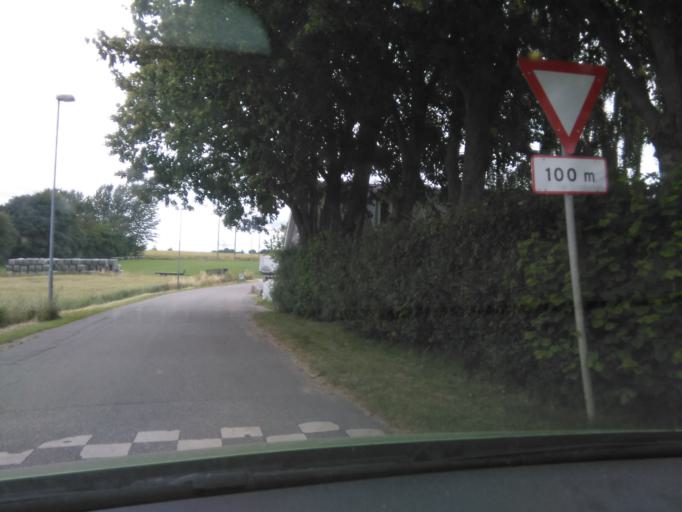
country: DK
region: Central Jutland
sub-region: Arhus Kommune
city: Marslet
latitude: 56.0288
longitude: 10.1436
